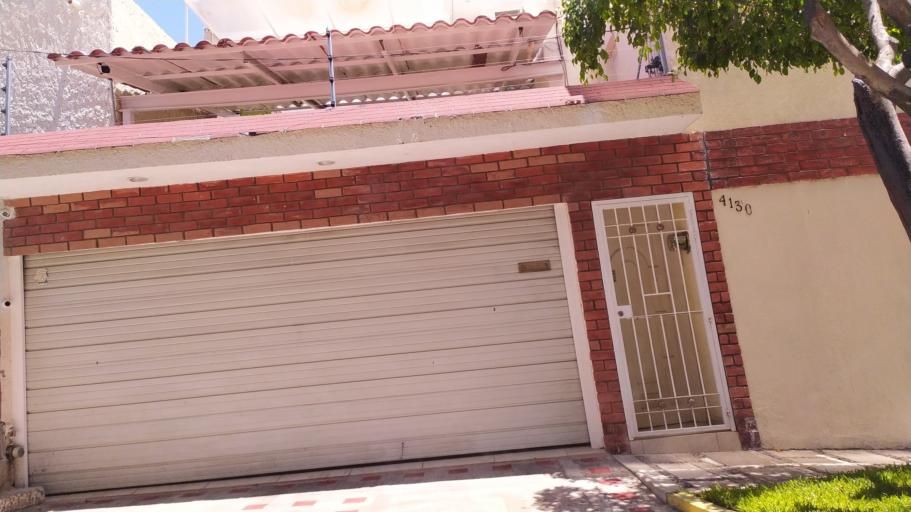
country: MX
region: Jalisco
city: Guadalajara
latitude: 20.6837
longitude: -103.4109
